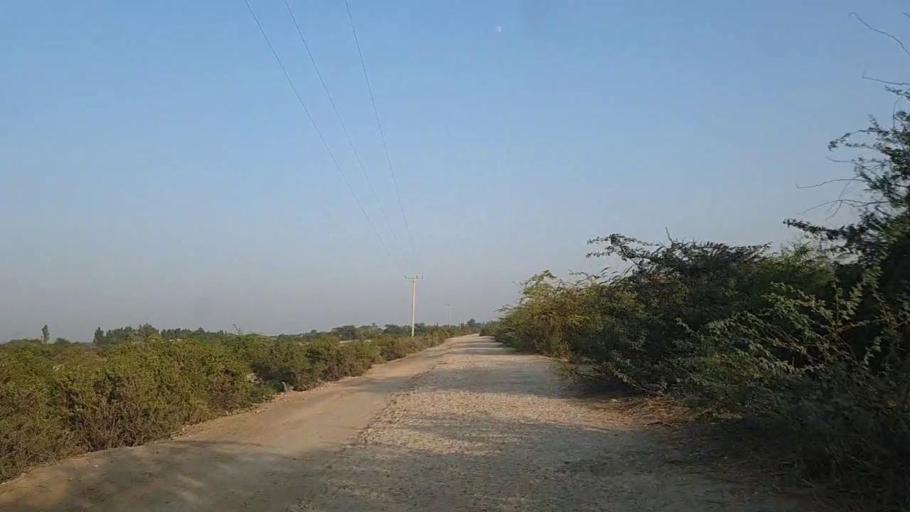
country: PK
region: Sindh
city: Keti Bandar
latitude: 24.2766
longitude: 67.6602
